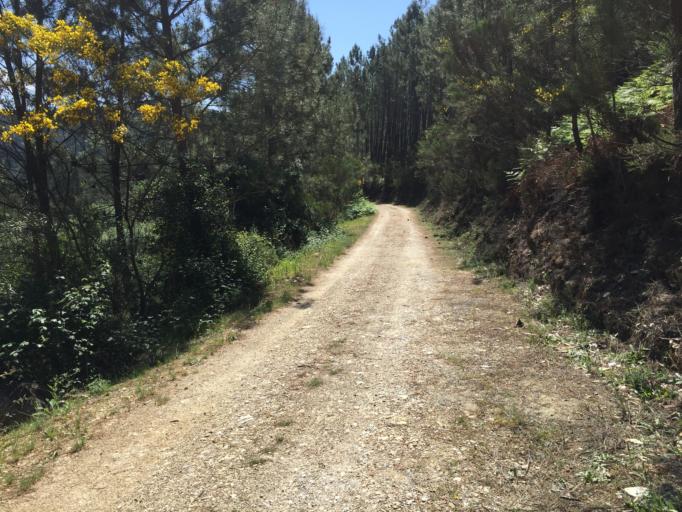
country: PT
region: Coimbra
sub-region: Pampilhosa da Serra
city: Pampilhosa da Serra
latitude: 40.0750
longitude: -7.7771
